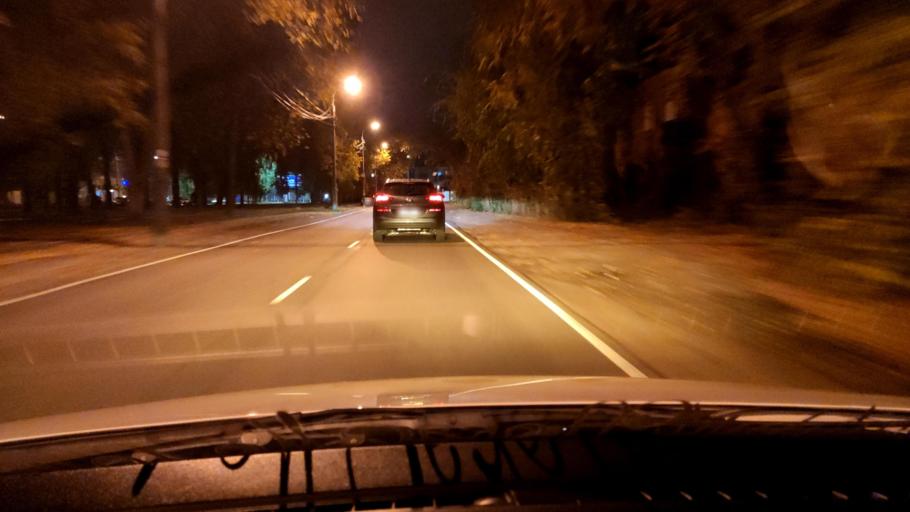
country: RU
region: Voronezj
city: Voronezh
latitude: 51.6769
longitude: 39.1672
